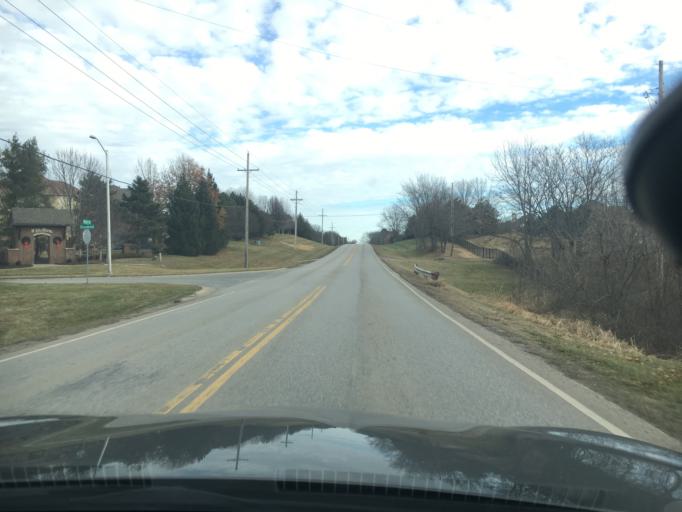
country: US
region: Kansas
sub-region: Johnson County
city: Leawood
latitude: 38.8547
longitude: -94.6449
